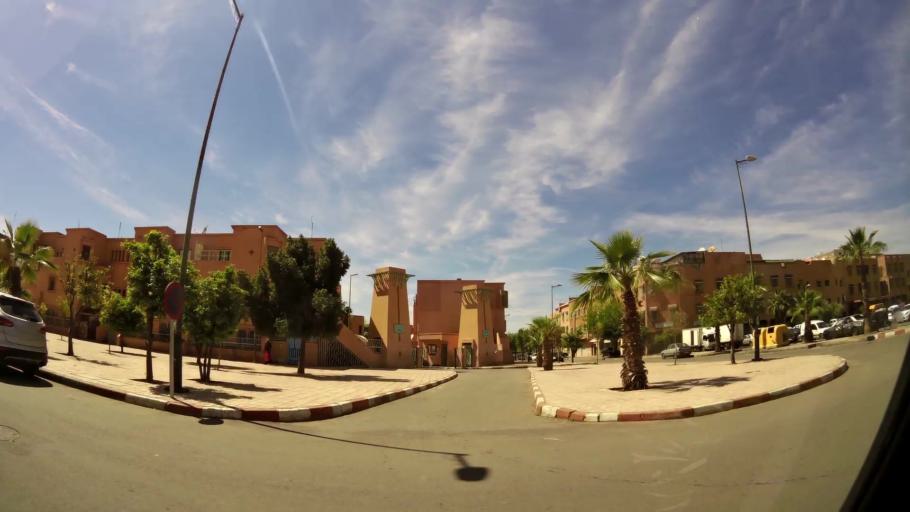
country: MA
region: Marrakech-Tensift-Al Haouz
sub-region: Marrakech
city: Marrakesh
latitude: 31.6093
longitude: -7.9705
